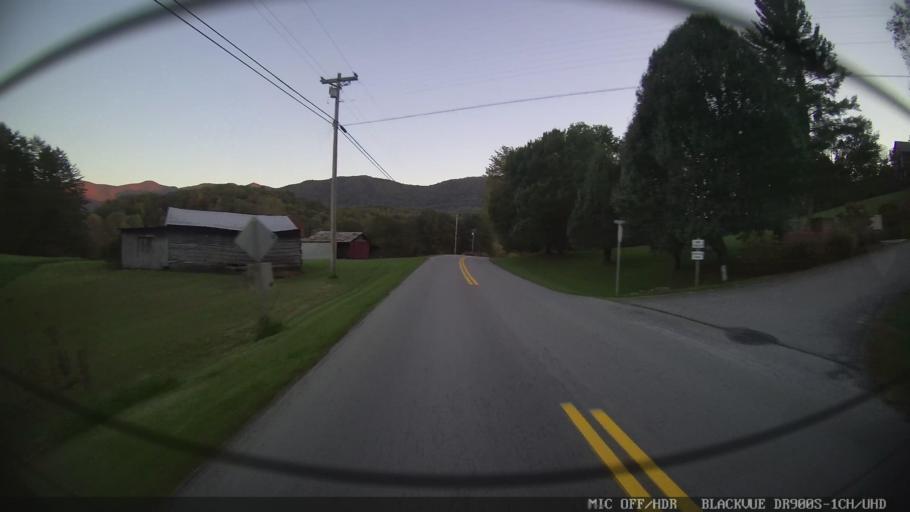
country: US
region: Georgia
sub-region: Union County
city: Blairsville
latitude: 34.9062
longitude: -83.8660
